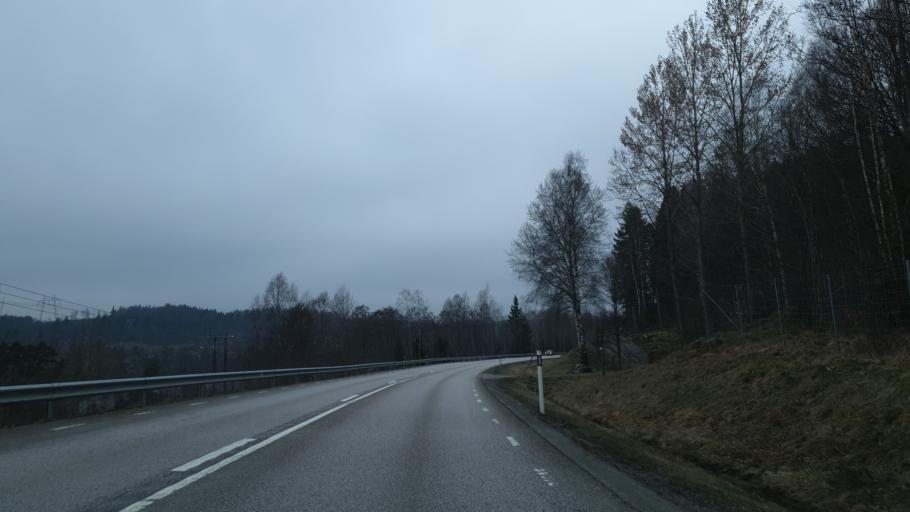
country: SE
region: Vaestra Goetaland
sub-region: Harryda Kommun
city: Hindas
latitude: 57.6263
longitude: 12.4144
